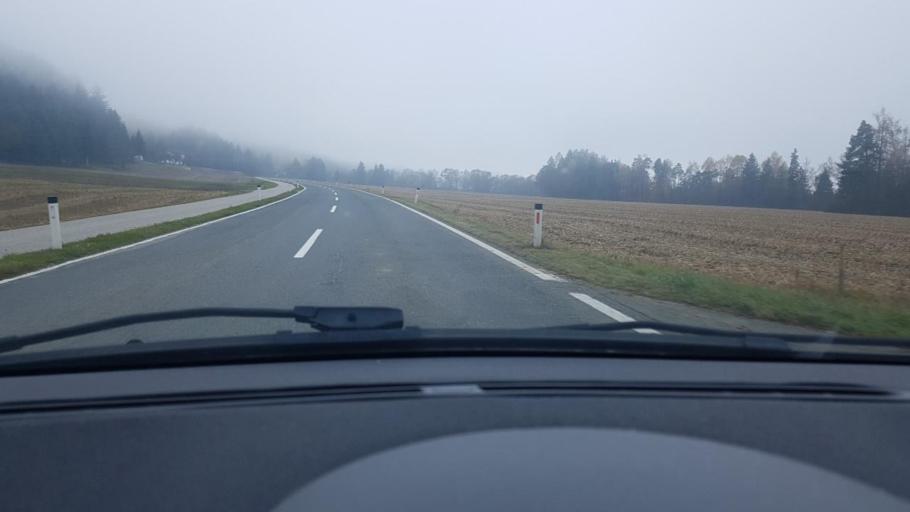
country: AT
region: Carinthia
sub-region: Politischer Bezirk Volkermarkt
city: Neuhaus
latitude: 46.6450
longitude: 14.8695
